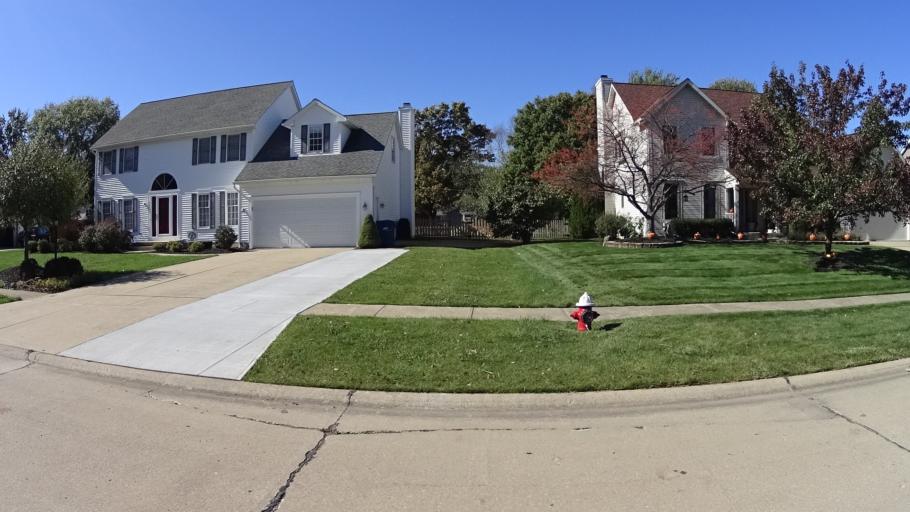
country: US
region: Ohio
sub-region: Lorain County
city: Amherst
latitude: 41.4078
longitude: -82.2130
